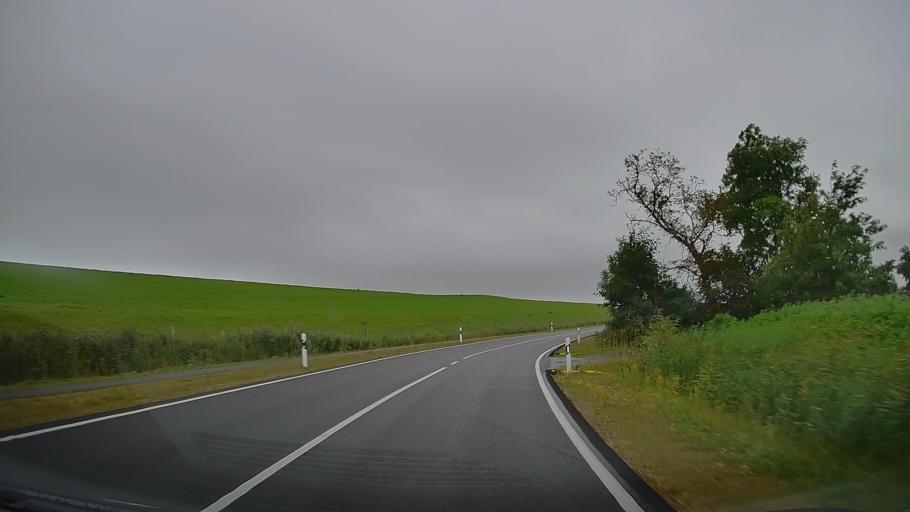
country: DE
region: Schleswig-Holstein
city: Brokdorf
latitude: 53.8726
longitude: 9.2970
